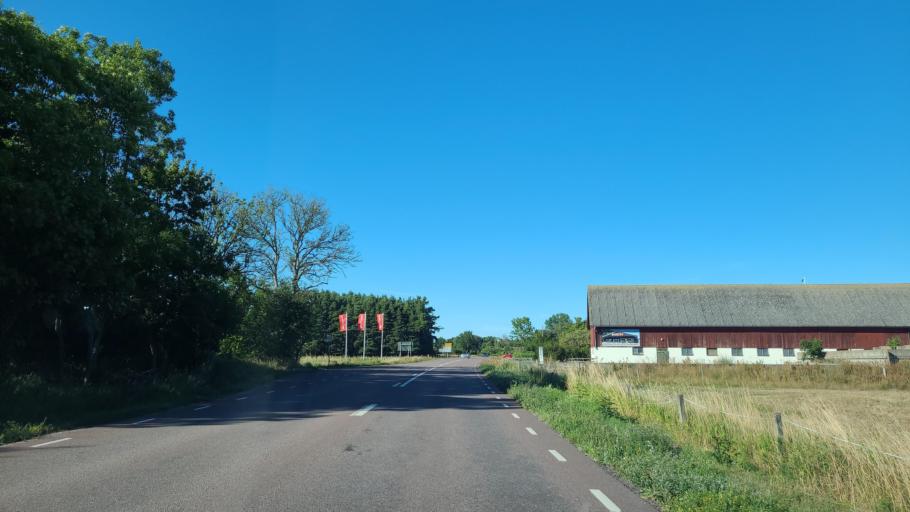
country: SE
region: Kalmar
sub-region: Borgholms Kommun
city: Borgholm
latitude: 57.1868
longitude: 17.0299
